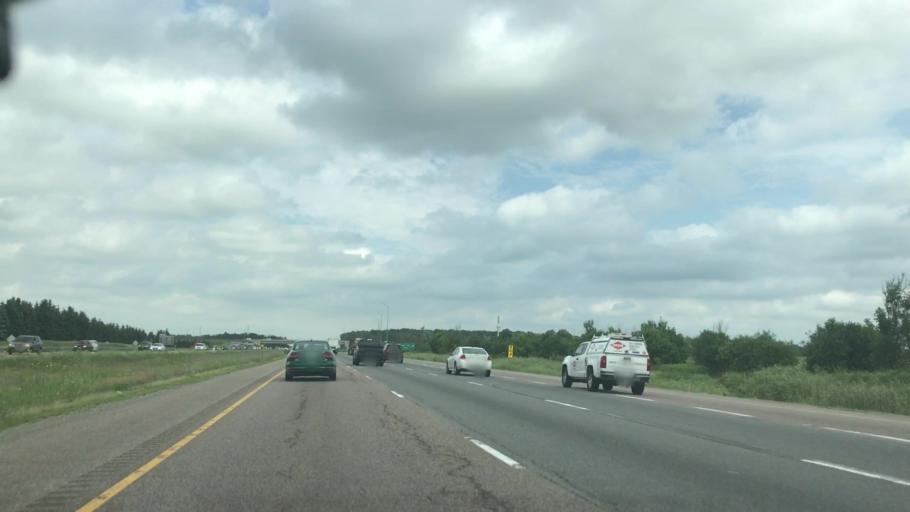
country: CA
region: Ontario
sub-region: York
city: Richmond Hill
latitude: 43.8939
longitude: -79.3823
